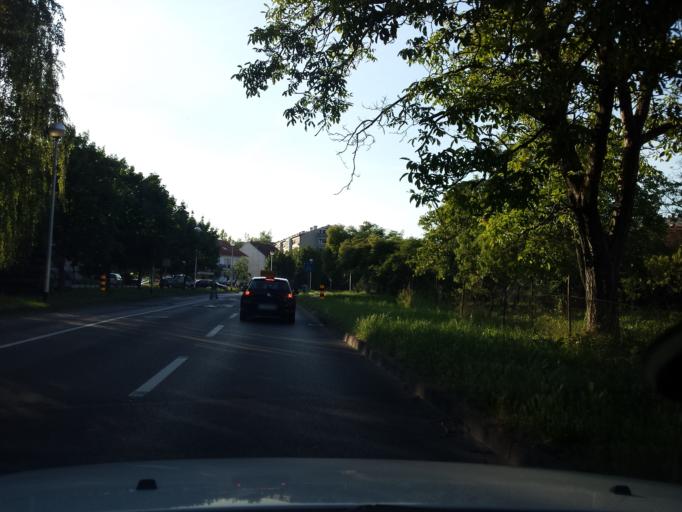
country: HR
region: Grad Zagreb
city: Jankomir
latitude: 45.7991
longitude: 15.8939
